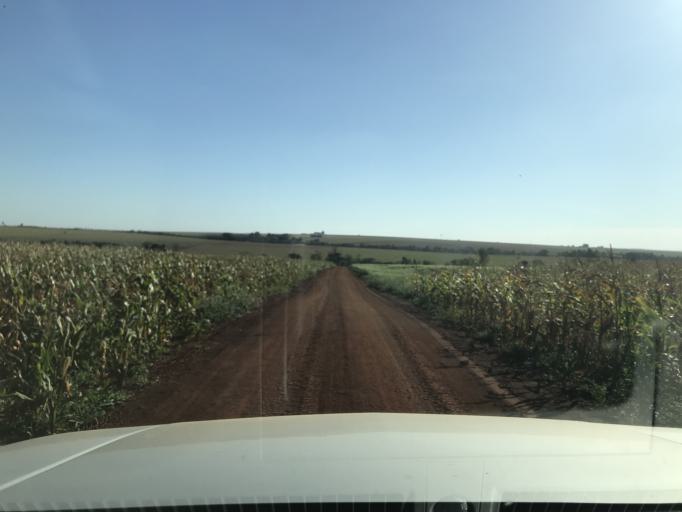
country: BR
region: Parana
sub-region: Palotina
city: Palotina
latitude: -24.2274
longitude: -53.8080
